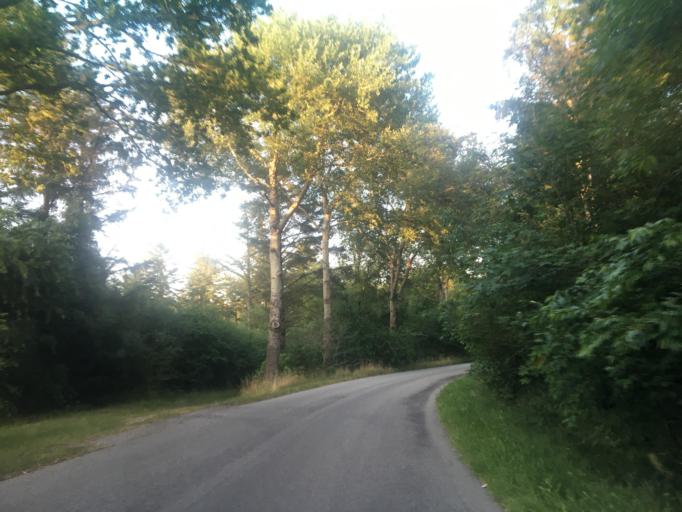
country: DK
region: North Denmark
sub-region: Thisted Kommune
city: Hurup
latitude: 56.8536
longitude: 8.3662
